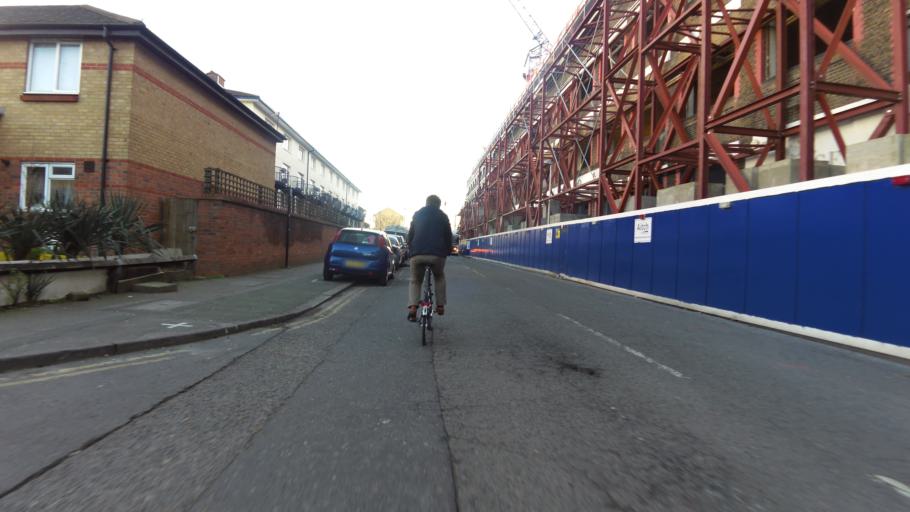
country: GB
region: England
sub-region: Greater London
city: Poplar
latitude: 51.4825
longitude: -0.0352
